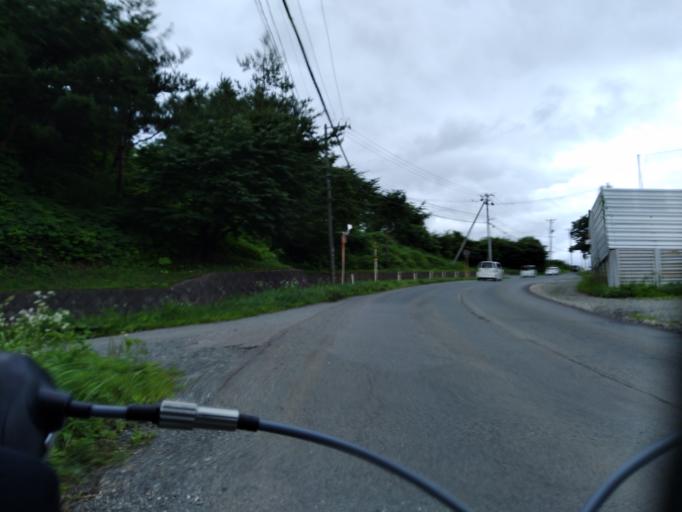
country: JP
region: Iwate
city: Morioka-shi
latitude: 39.7899
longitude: 141.1141
